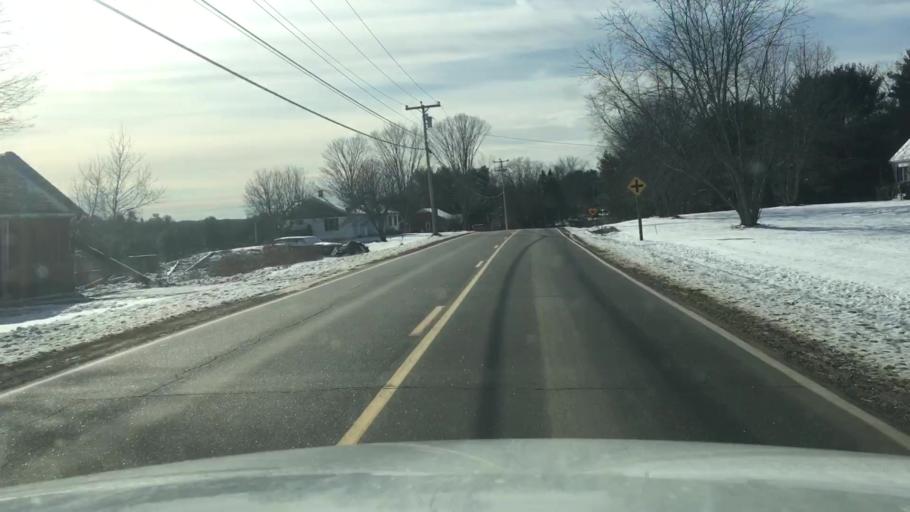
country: US
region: Maine
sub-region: Lincoln County
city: Wiscasset
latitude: 43.9650
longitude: -69.6986
